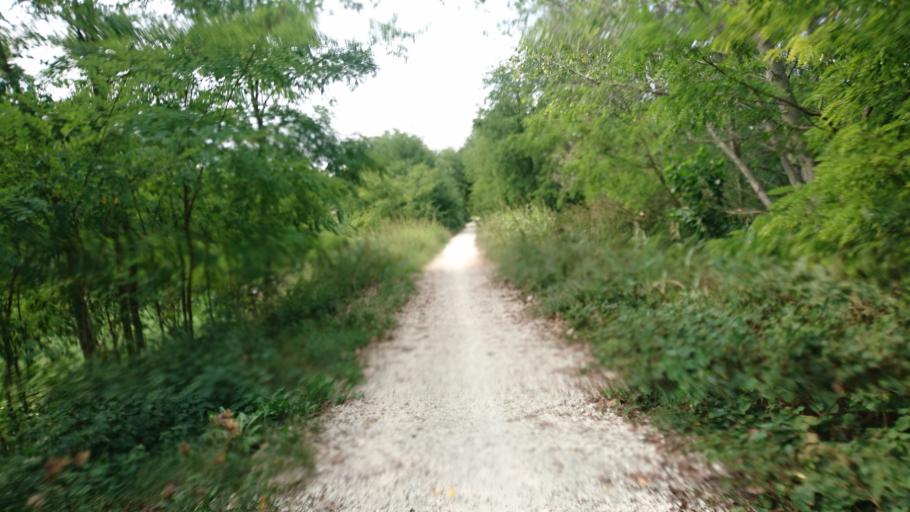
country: IT
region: Veneto
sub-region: Provincia di Padova
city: Saletto
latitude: 45.4705
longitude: 11.8541
